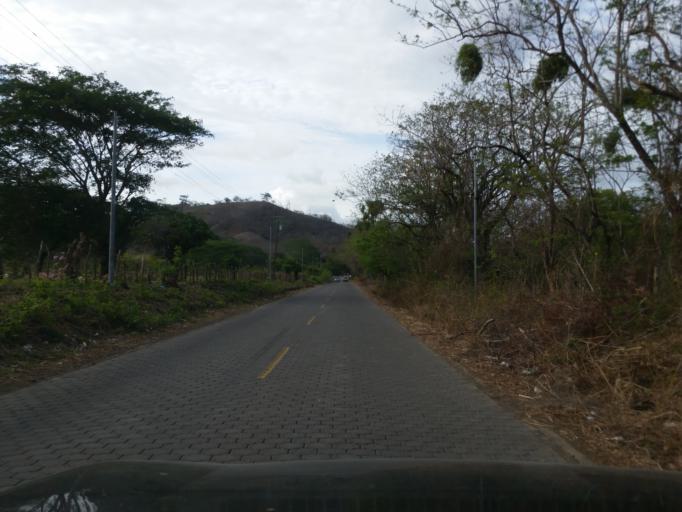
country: NI
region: Rivas
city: Tola
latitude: 11.4053
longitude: -85.9559
